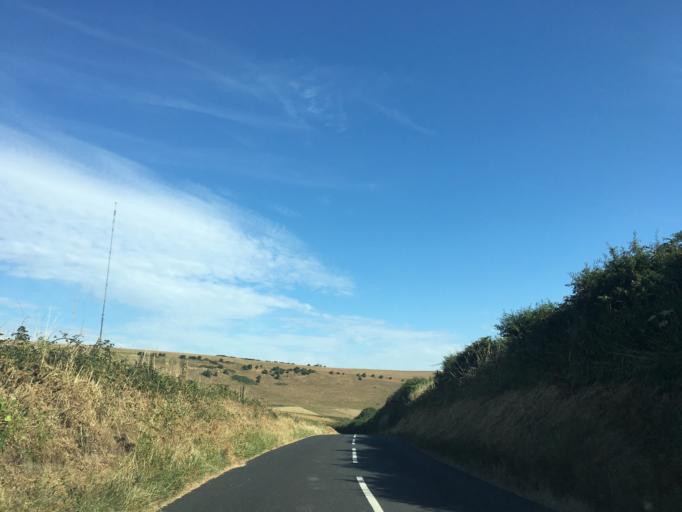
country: GB
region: England
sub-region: Isle of Wight
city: Chale
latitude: 50.6429
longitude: -1.3196
